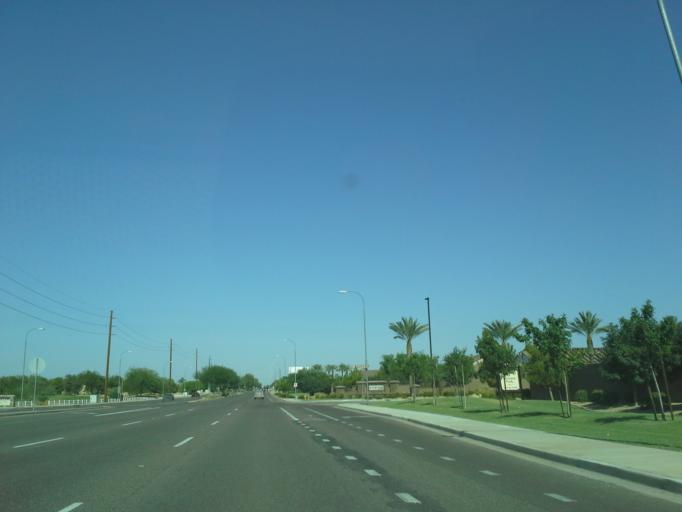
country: US
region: Arizona
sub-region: Maricopa County
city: Sun Lakes
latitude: 33.2185
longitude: -111.8357
